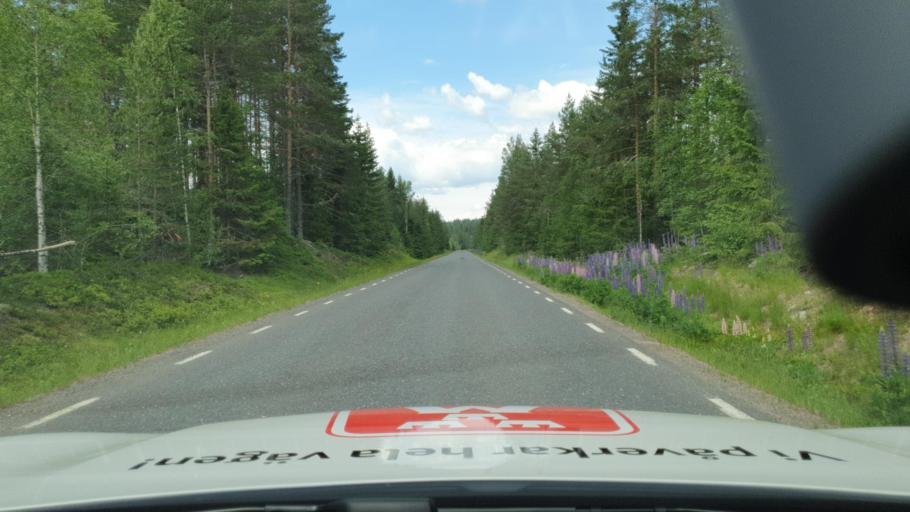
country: SE
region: Vaermland
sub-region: Torsby Kommun
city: Torsby
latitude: 60.5174
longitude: 12.8290
